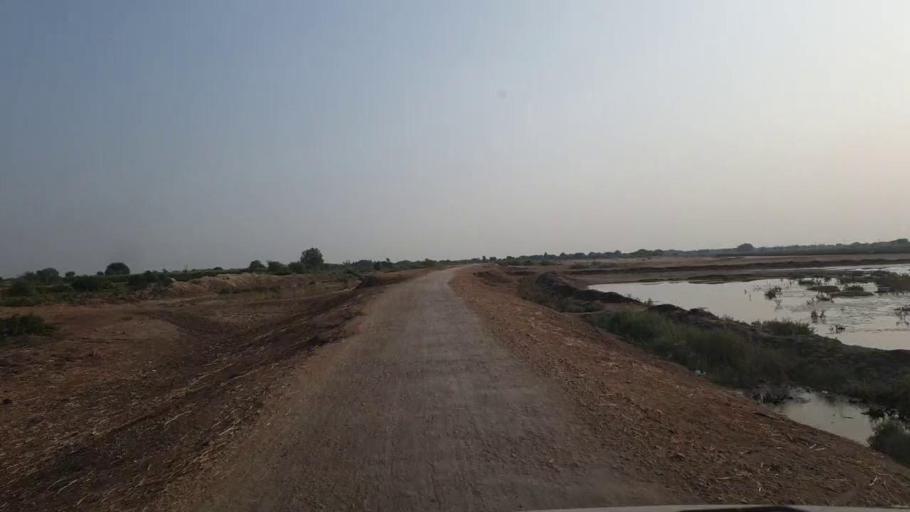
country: PK
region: Sindh
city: Rajo Khanani
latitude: 25.0469
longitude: 68.7661
